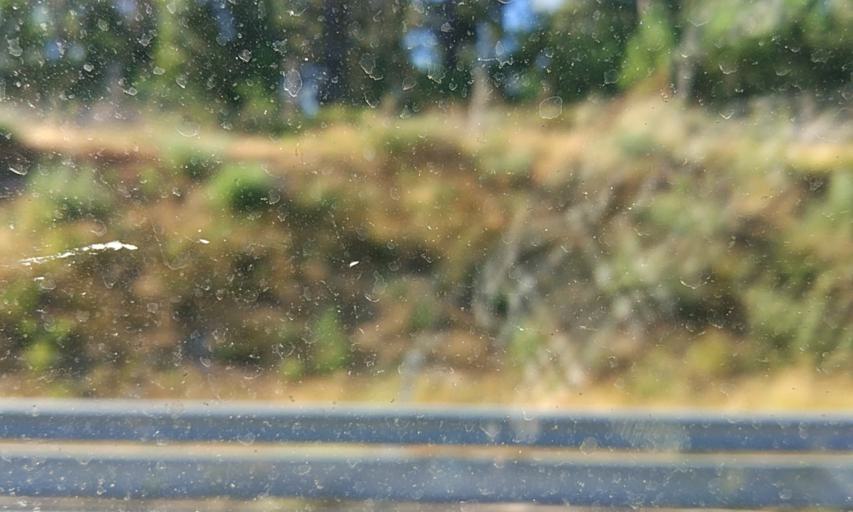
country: PT
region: Vila Real
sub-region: Sabrosa
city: Sabrosa
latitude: 41.3266
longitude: -7.6304
